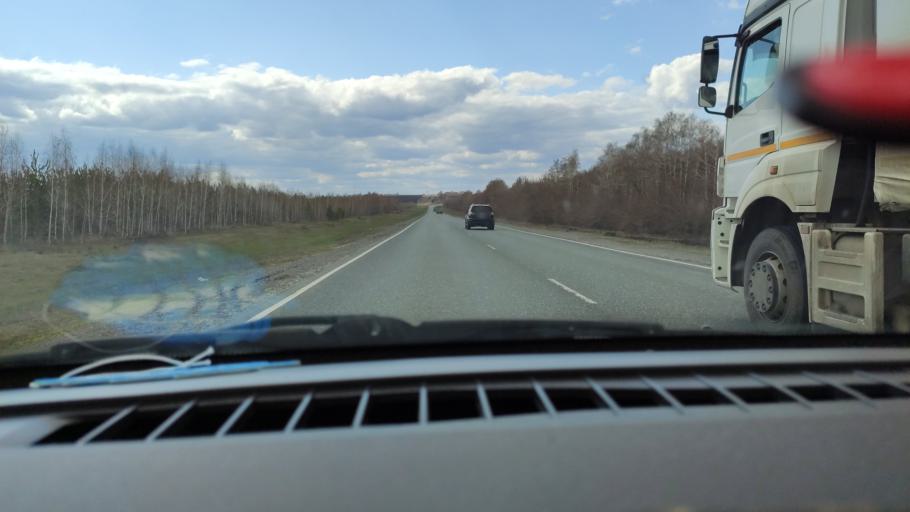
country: RU
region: Saratov
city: Balakovo
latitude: 52.1423
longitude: 47.8025
